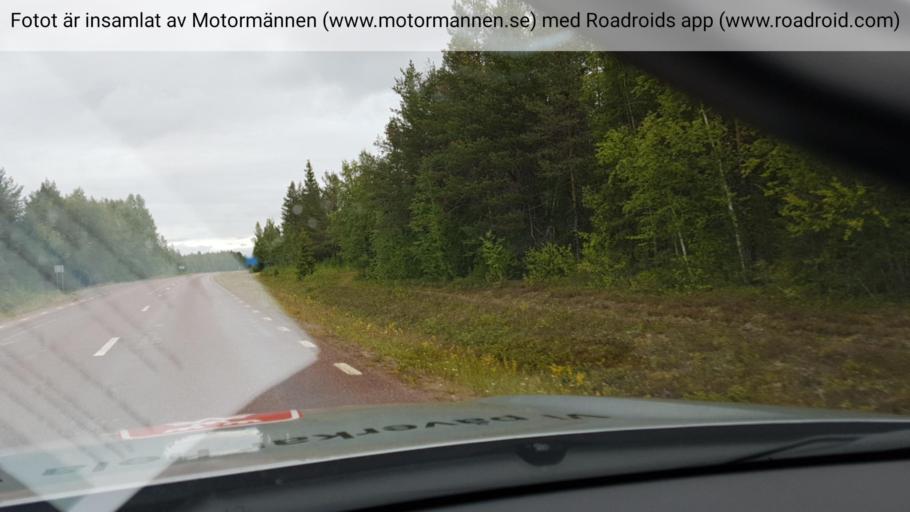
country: SE
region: Norrbotten
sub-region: Pajala Kommun
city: Pajala
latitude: 67.1352
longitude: 22.6087
